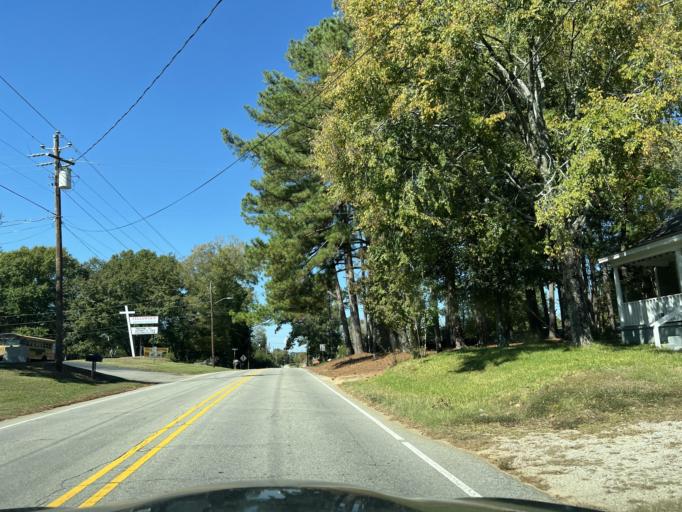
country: US
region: North Carolina
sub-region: Johnston County
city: Clayton
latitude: 35.6604
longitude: -78.4688
